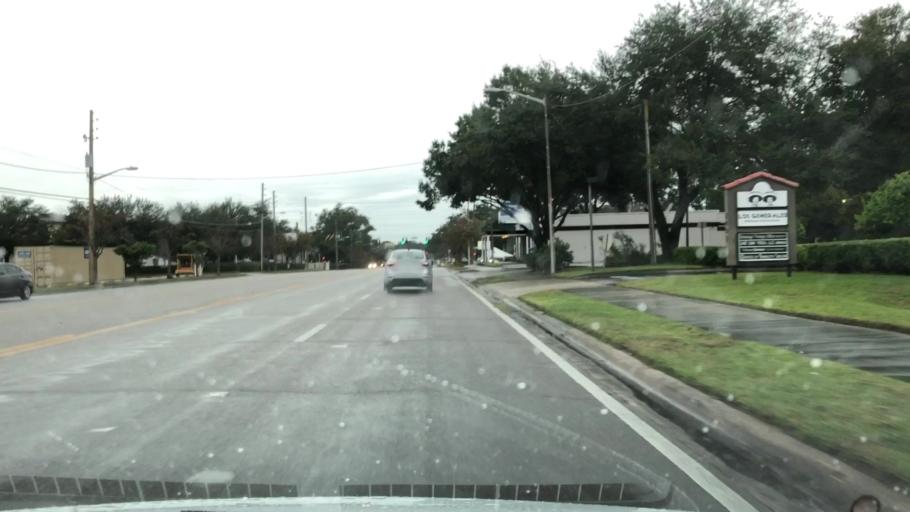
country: US
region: Florida
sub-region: Orange County
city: Conway
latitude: 28.5242
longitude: -81.3458
